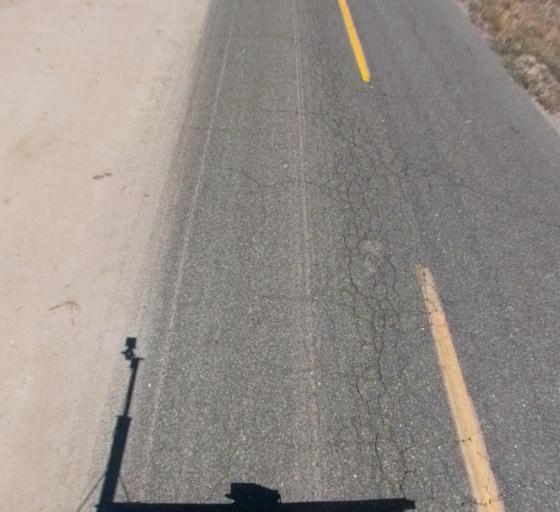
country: US
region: California
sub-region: Fresno County
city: Biola
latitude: 36.8450
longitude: -120.0011
